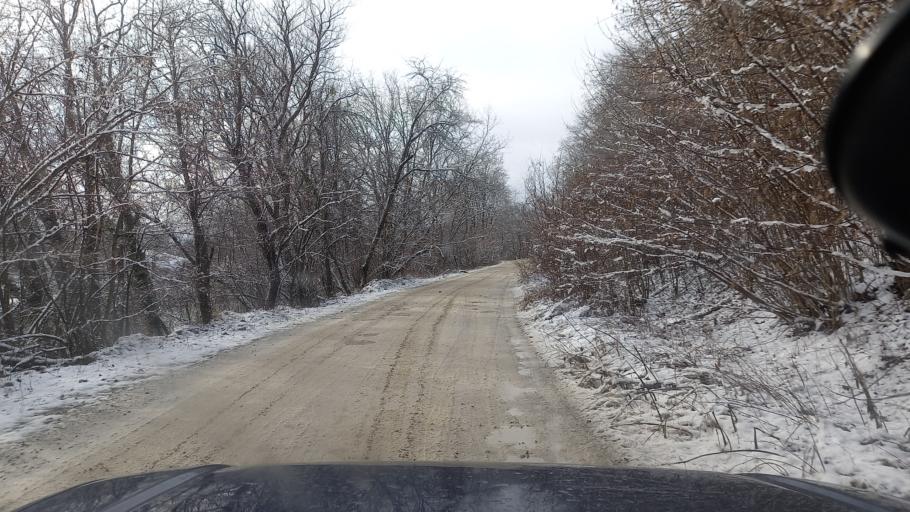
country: RU
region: Adygeya
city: Kamennomostskiy
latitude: 44.2402
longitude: 40.1960
